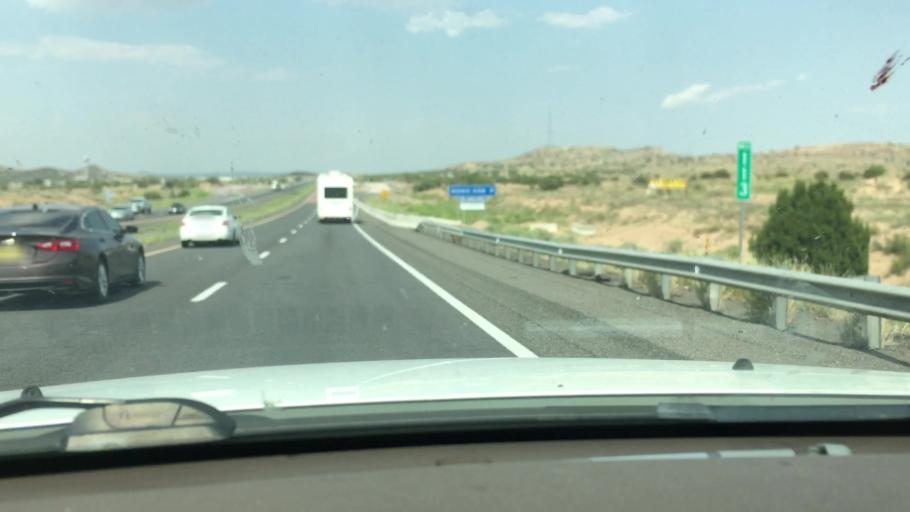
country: US
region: New Mexico
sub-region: Cibola County
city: Laguna
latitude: 35.0287
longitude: -107.3869
